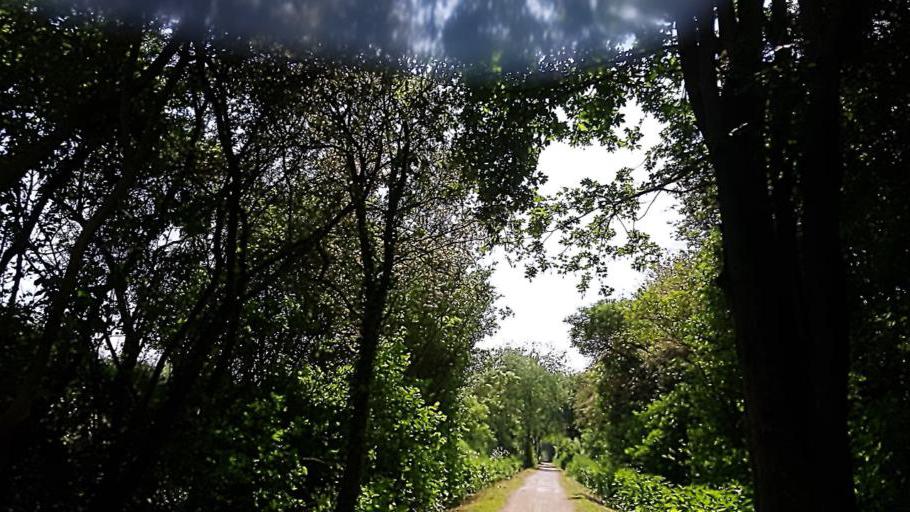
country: BE
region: Wallonia
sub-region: Province du Hainaut
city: Peruwelz
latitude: 50.4929
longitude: 3.5683
